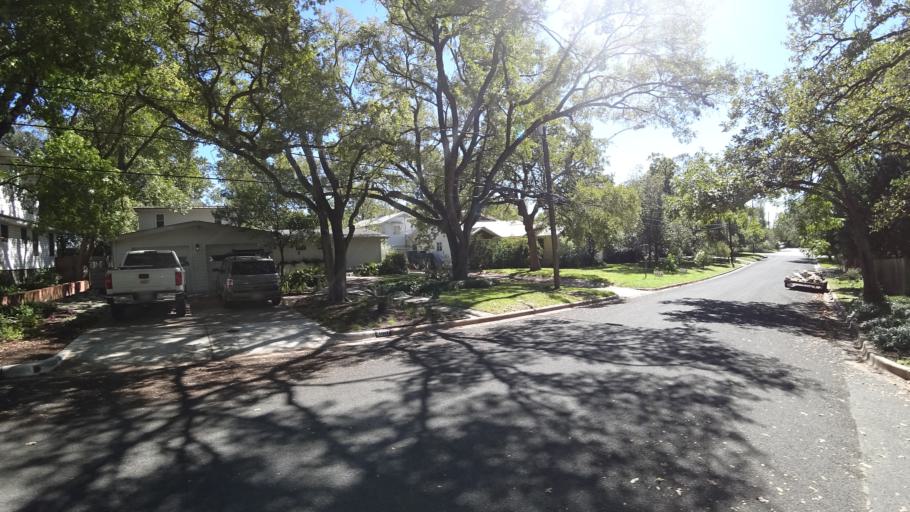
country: US
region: Texas
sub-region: Travis County
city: Austin
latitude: 30.2934
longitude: -97.7101
